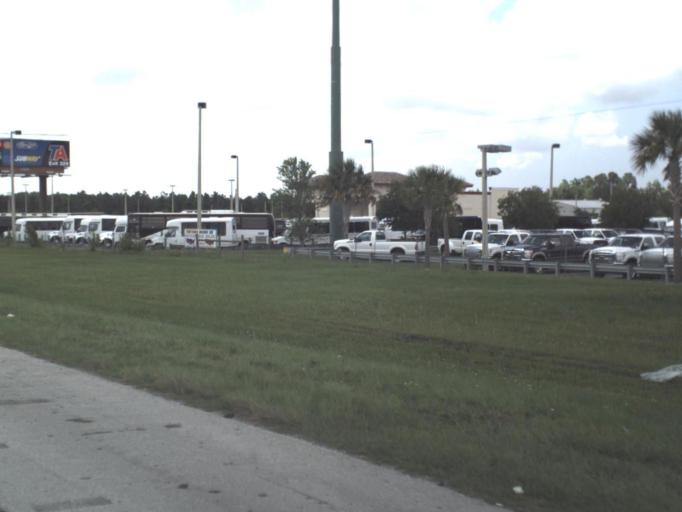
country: US
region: Florida
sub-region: Saint Johns County
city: Saint Augustine
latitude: 29.9264
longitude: -81.4168
